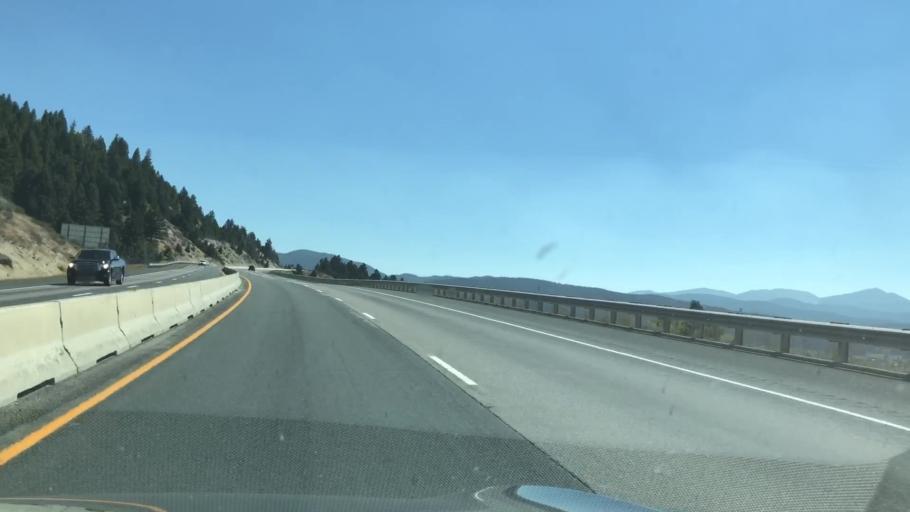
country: US
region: Montana
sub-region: Silver Bow County
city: Butte
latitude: 45.9378
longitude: -112.4560
